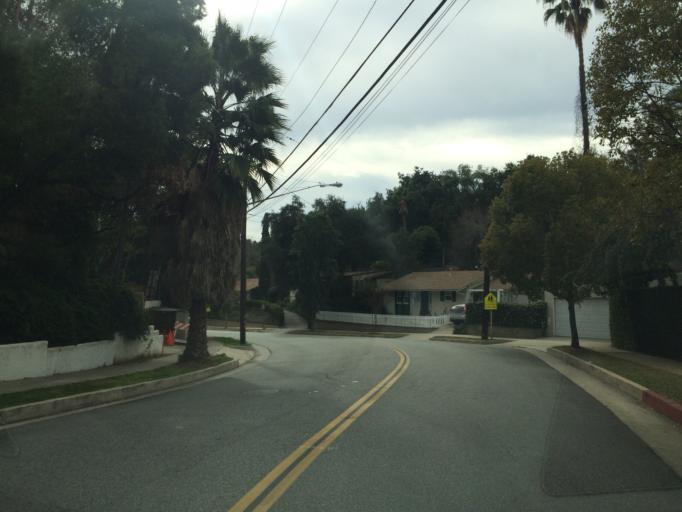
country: US
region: California
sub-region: Los Angeles County
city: South Pasadena
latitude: 34.1109
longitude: -118.1573
